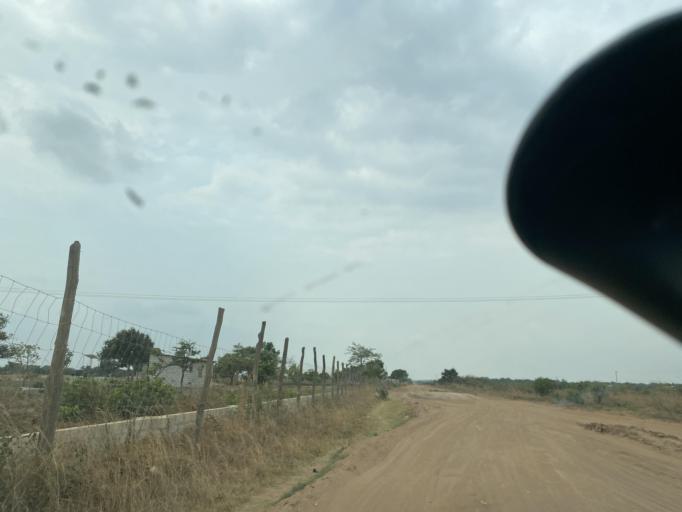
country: ZM
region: Lusaka
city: Lusaka
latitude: -15.2166
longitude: 28.3382
